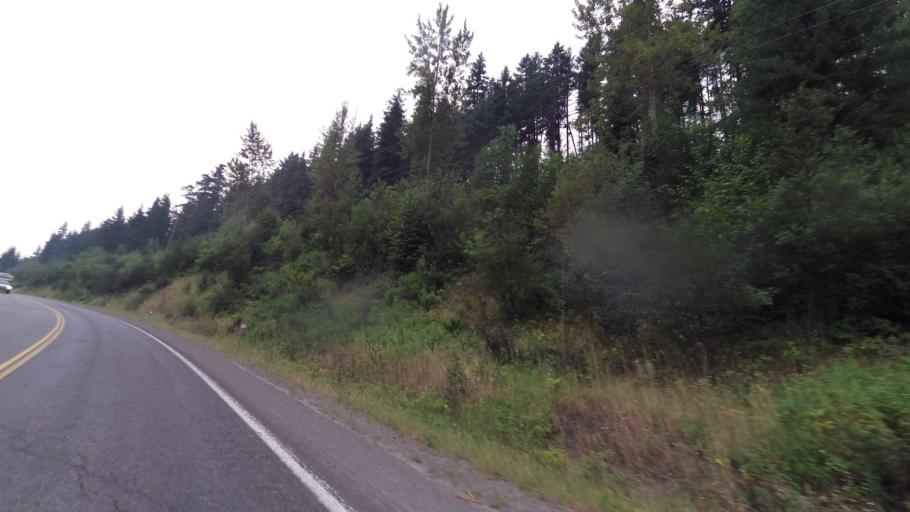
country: CA
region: British Columbia
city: Kamloops
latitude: 51.3873
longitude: -120.2011
